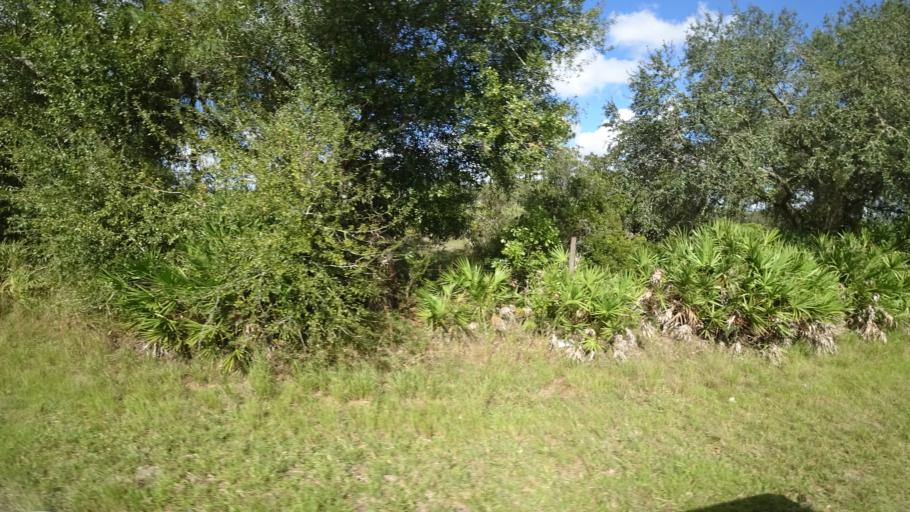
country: US
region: Florida
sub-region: Sarasota County
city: Lake Sarasota
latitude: 27.3627
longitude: -82.1529
